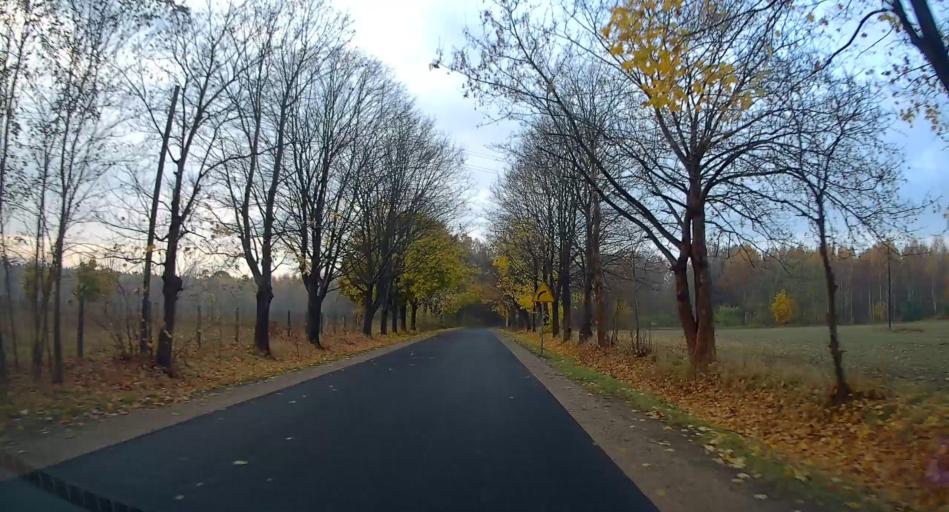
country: PL
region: Masovian Voivodeship
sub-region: Powiat zyrardowski
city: Puszcza Marianska
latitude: 51.9438
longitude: 20.3704
